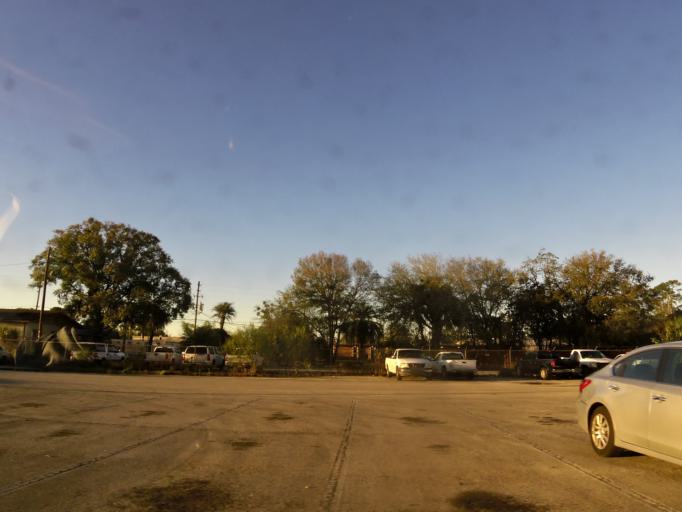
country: US
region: Florida
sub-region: Duval County
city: Jacksonville
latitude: 30.3396
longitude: -81.7093
